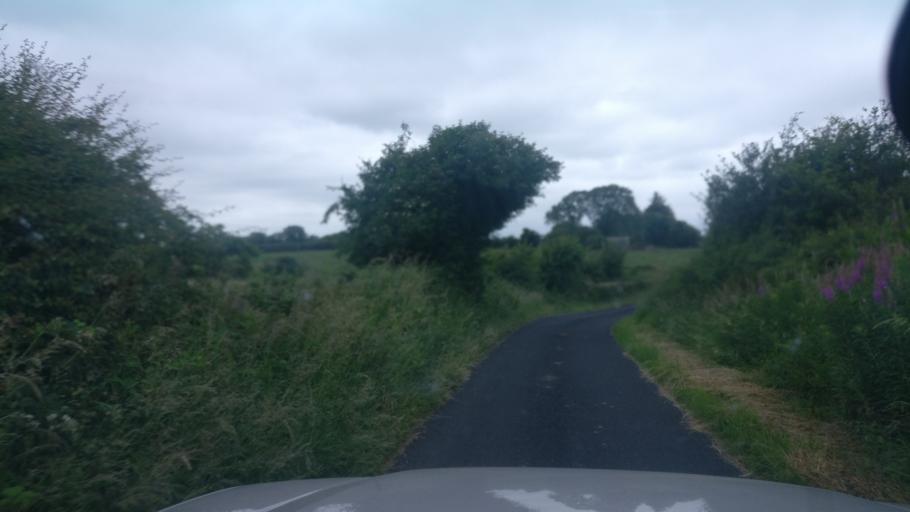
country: IE
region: Connaught
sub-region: County Galway
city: Ballinasloe
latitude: 53.2943
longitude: -8.3764
